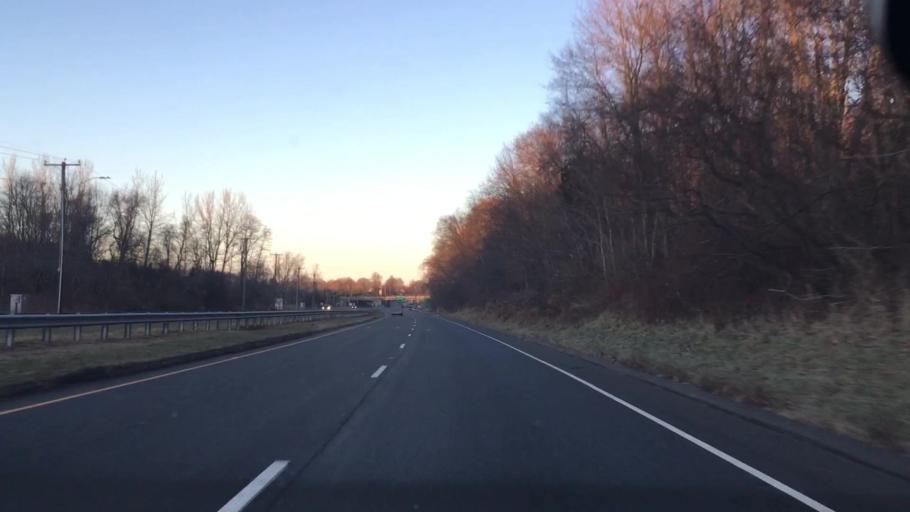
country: US
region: Connecticut
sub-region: Hartford County
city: Kensington
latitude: 41.6187
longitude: -72.7423
